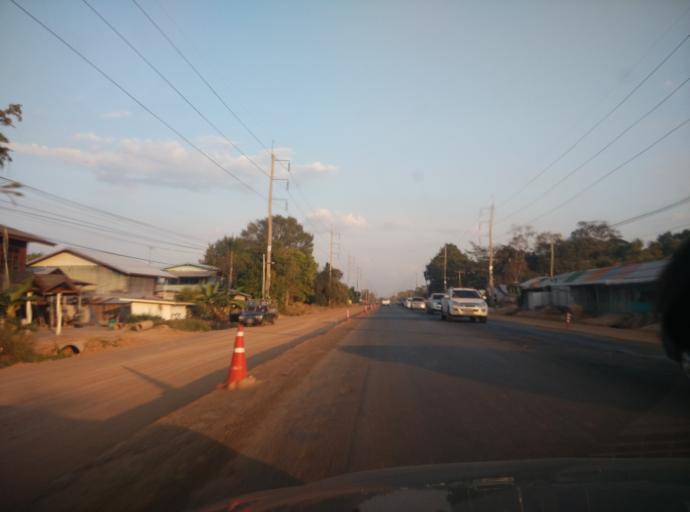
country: TH
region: Sisaket
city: Uthumphon Phisai
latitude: 15.1506
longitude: 104.2118
